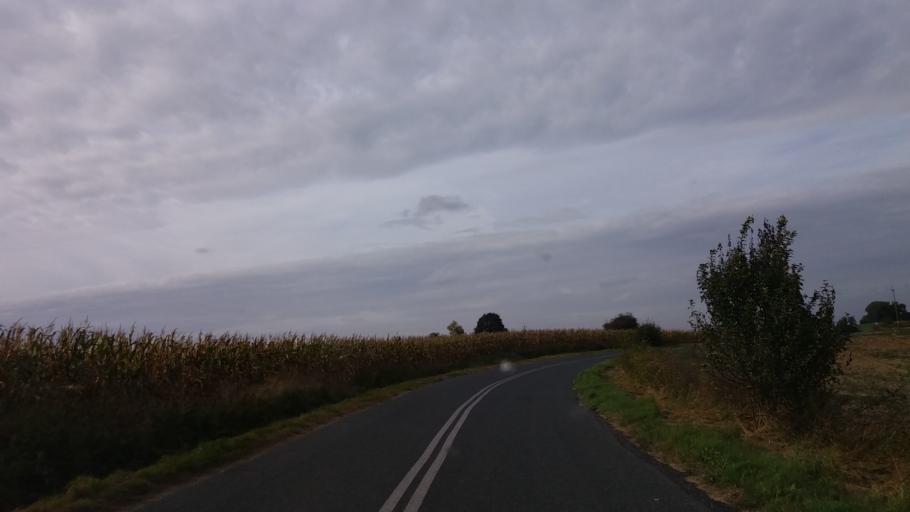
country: PL
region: West Pomeranian Voivodeship
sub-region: Powiat choszczenski
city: Krzecin
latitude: 53.0441
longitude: 15.4930
